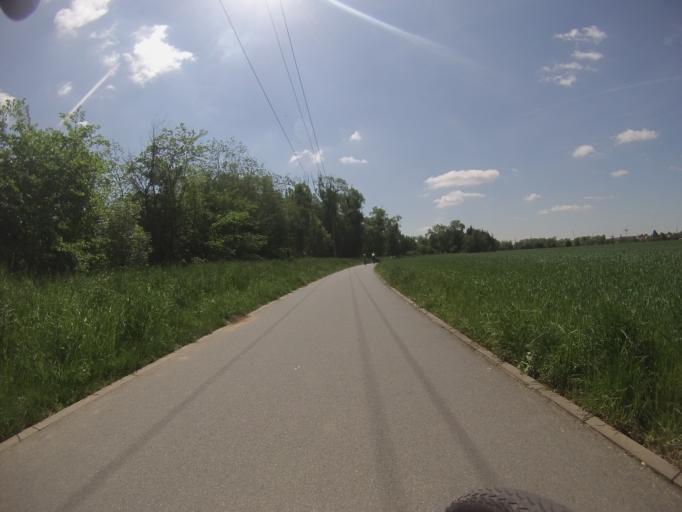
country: CZ
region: South Moravian
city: Modrice
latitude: 49.1497
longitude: 16.6285
